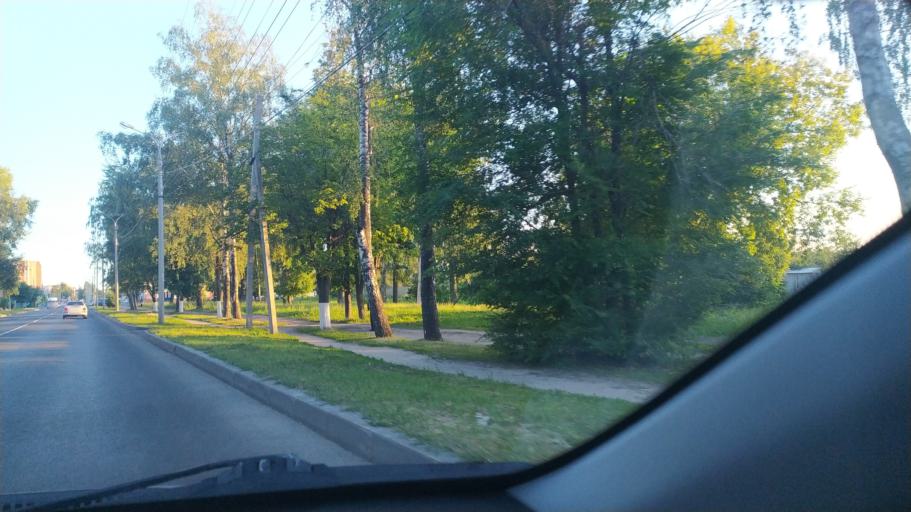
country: RU
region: Chuvashia
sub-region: Cheboksarskiy Rayon
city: Cheboksary
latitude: 56.1202
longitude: 47.2256
